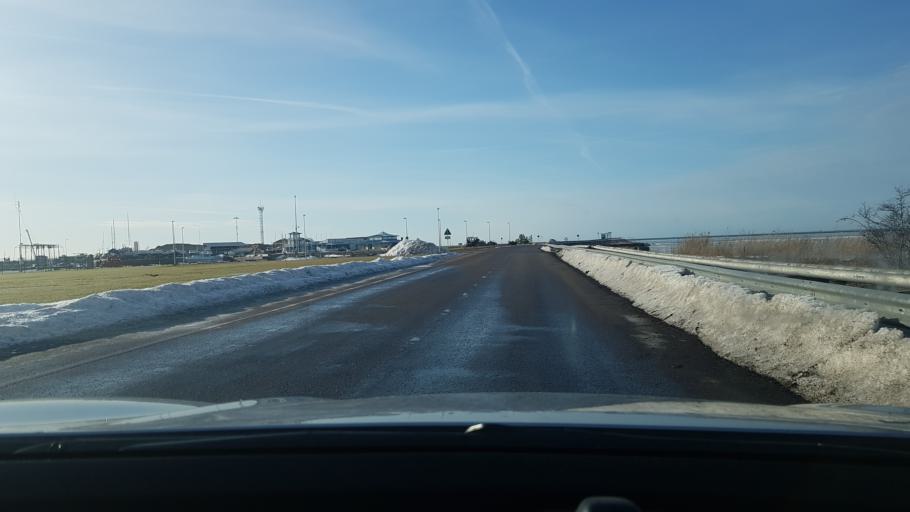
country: EE
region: Saare
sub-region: Kuressaare linn
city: Kuressaare
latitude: 58.2191
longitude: 22.5062
